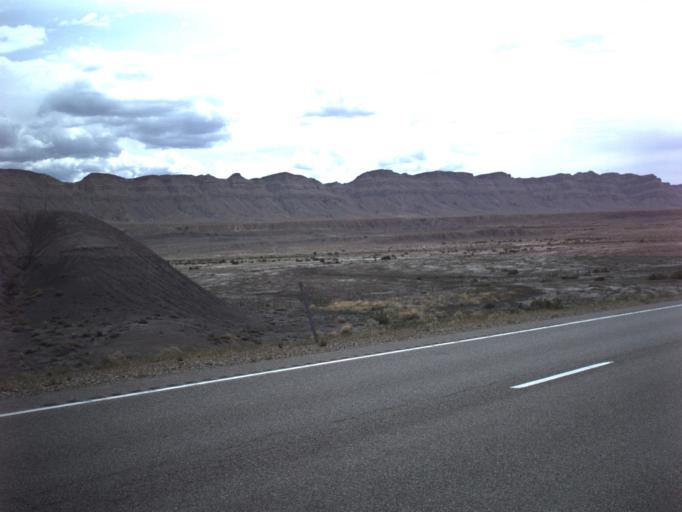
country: US
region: Utah
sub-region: Carbon County
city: East Carbon City
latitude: 39.3409
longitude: -110.3728
